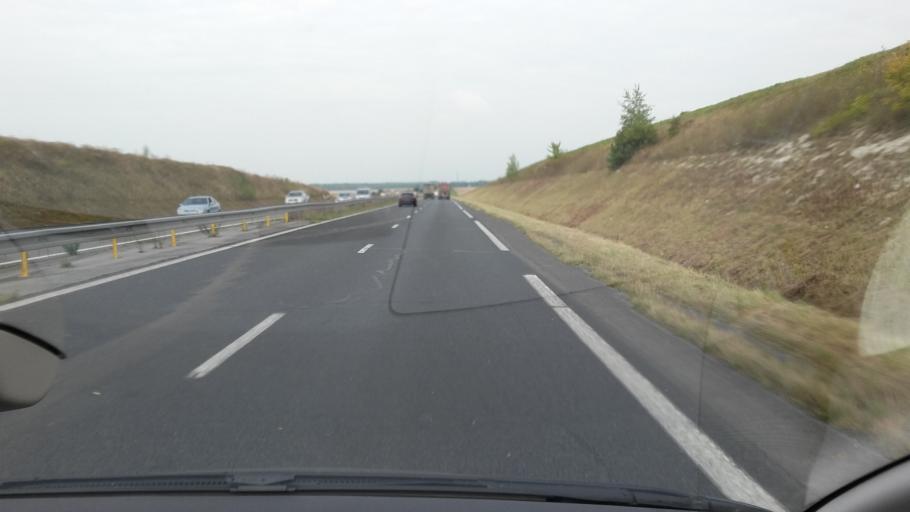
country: FR
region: Champagne-Ardenne
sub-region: Departement de la Marne
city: Warmeriville
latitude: 49.3676
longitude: 4.2127
